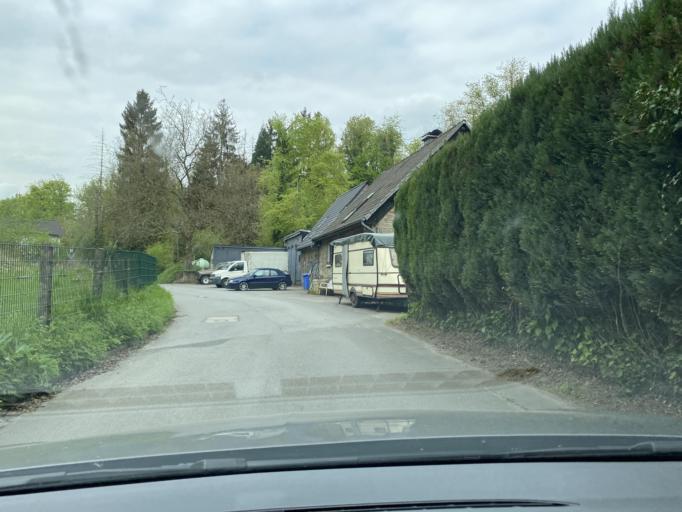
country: DE
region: North Rhine-Westphalia
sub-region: Regierungsbezirk Dusseldorf
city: Ratingen
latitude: 51.3196
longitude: 6.9052
